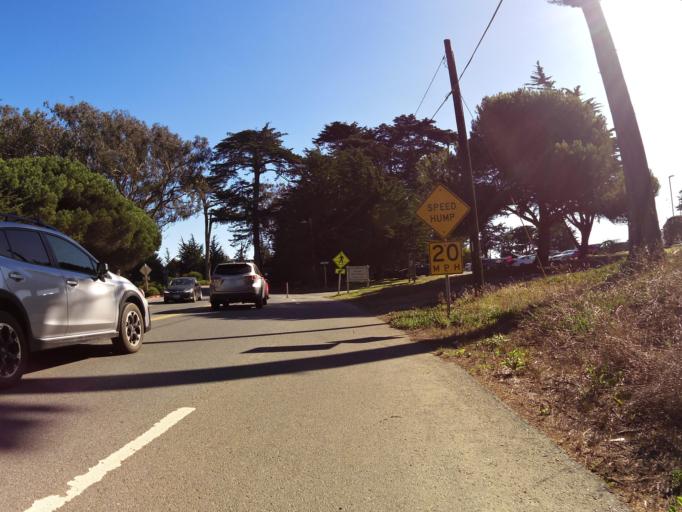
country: US
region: California
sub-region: San Francisco County
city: San Francisco
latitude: 37.7913
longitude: -122.4588
